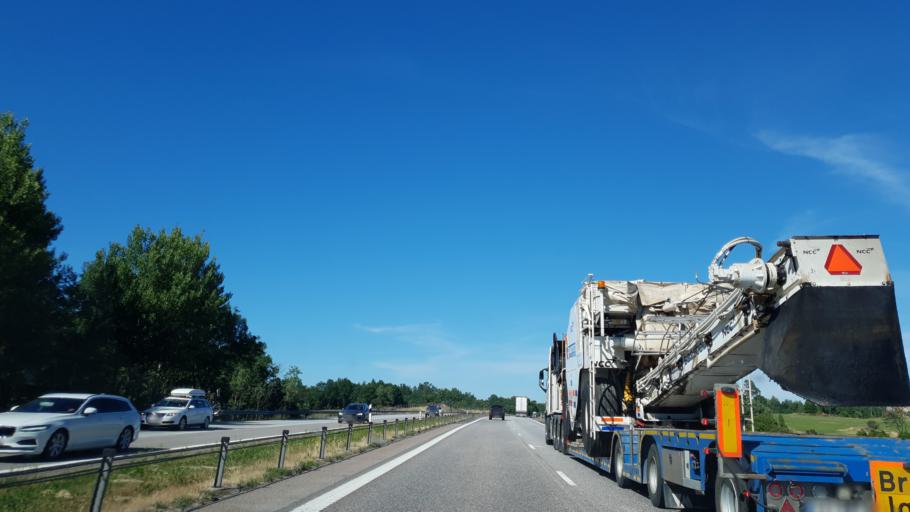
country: SE
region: OEstergoetland
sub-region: Odeshogs Kommun
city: OEdeshoeg
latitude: 58.1945
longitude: 14.6108
